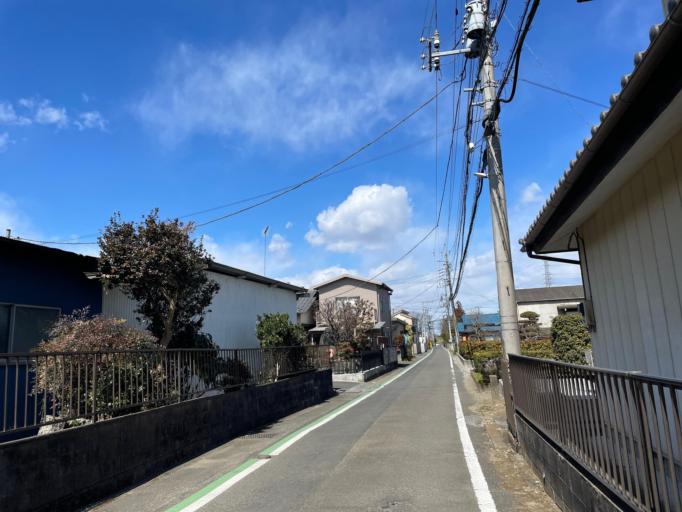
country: JP
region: Saitama
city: Sakado
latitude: 35.9852
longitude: 139.4102
